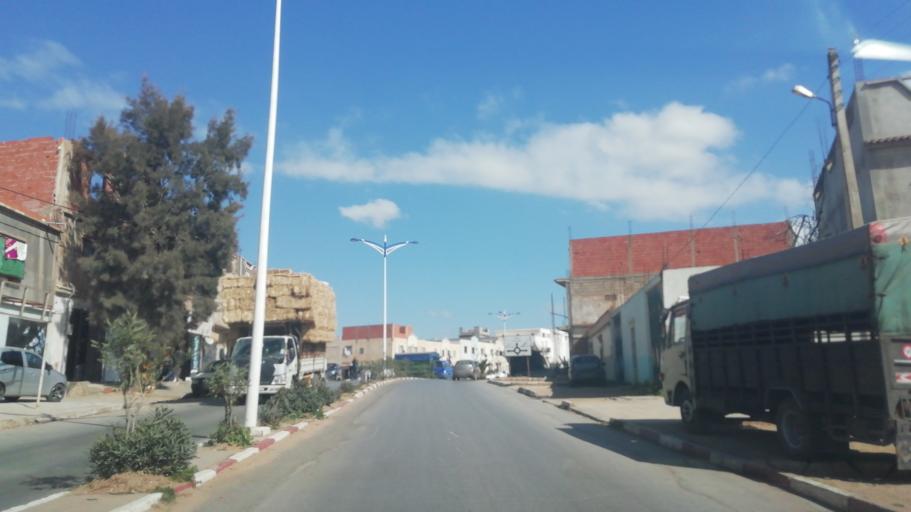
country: DZ
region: Mostaganem
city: Mostaganem
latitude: 35.9961
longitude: 0.3034
